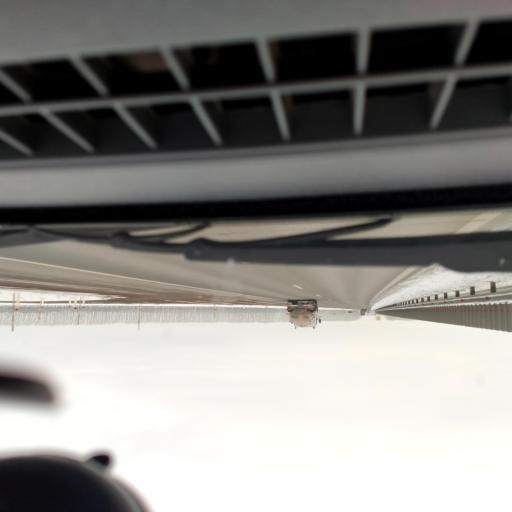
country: RU
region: Bashkortostan
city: Asanovo
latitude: 54.9811
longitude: 55.5552
